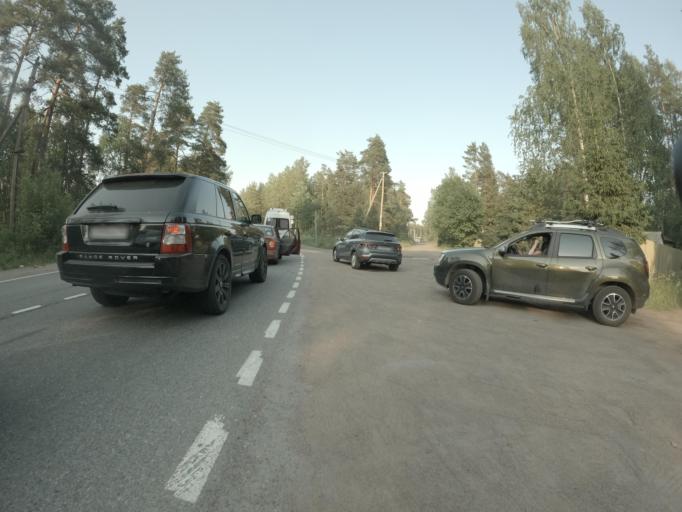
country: RU
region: Leningrad
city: Veshchevo
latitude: 60.4715
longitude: 29.2727
